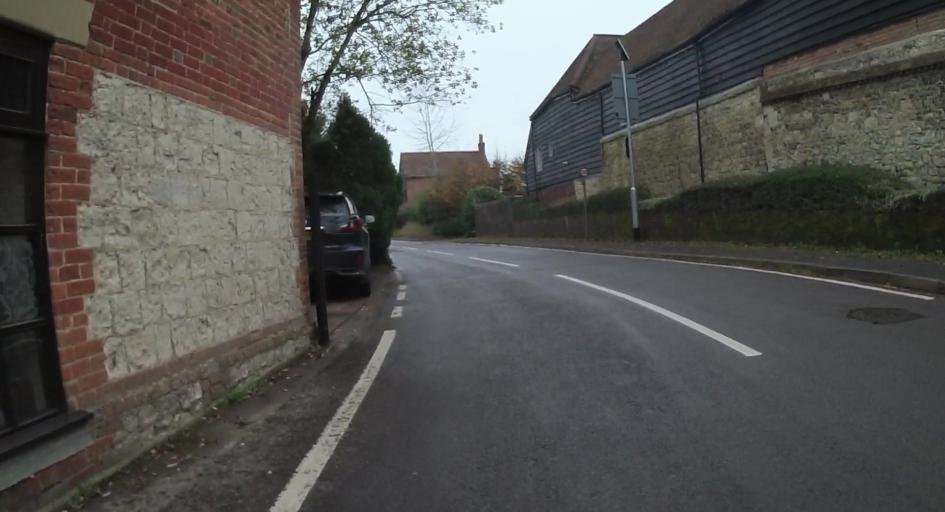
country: GB
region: England
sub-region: Hampshire
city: Kingsley
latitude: 51.1641
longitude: -0.8983
